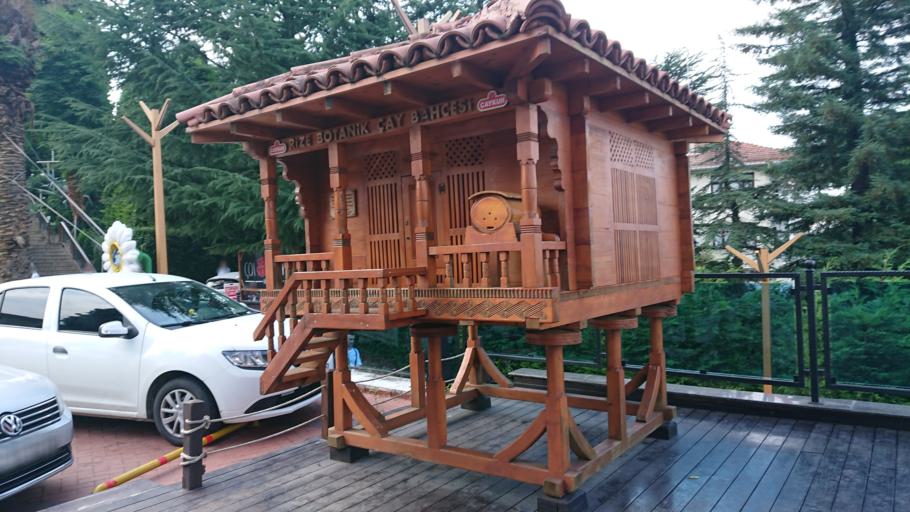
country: TR
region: Rize
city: Rize
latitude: 41.0210
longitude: 40.5114
